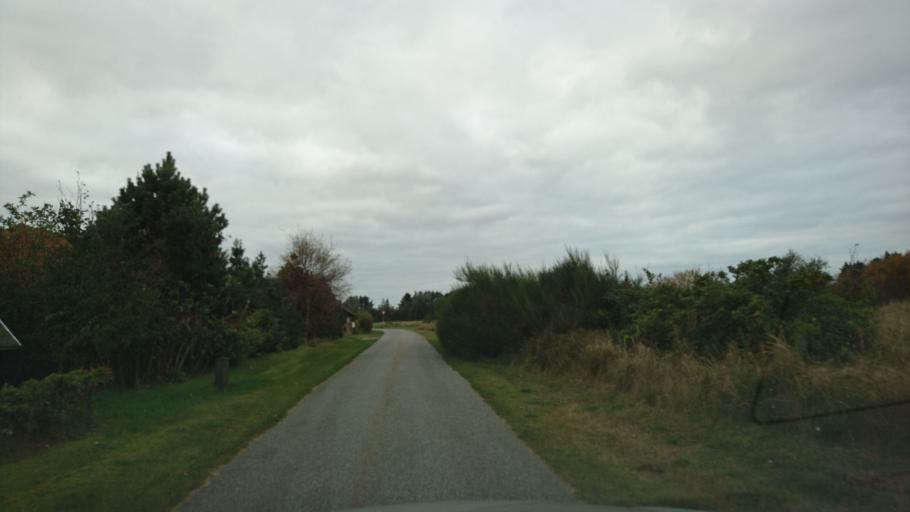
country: DK
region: North Denmark
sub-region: Frederikshavn Kommune
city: Skagen
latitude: 57.6626
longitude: 10.4628
